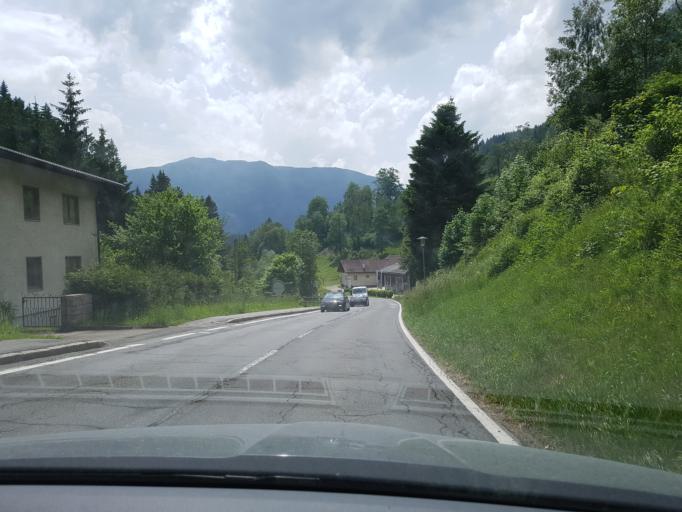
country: AT
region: Carinthia
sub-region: Politischer Bezirk Spittal an der Drau
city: Kleinkirchheim
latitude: 46.8081
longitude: 13.7629
